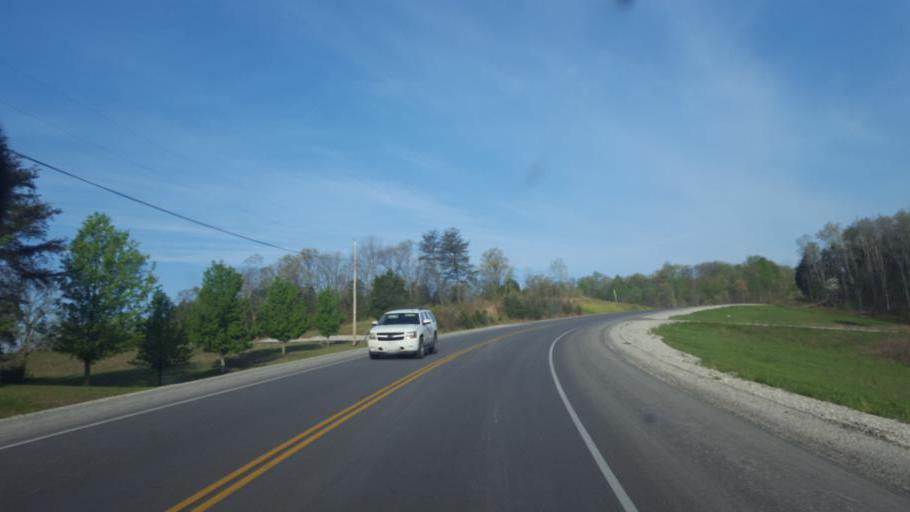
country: US
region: Kentucky
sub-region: Hart County
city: Munfordville
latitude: 37.2736
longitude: -85.9256
